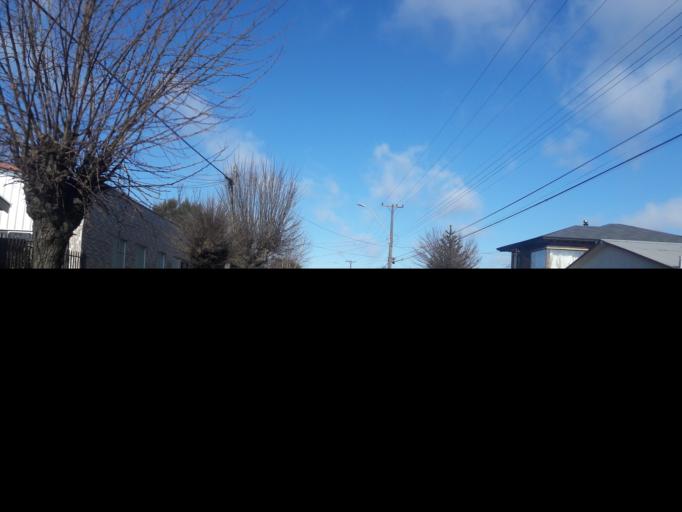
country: CL
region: Araucania
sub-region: Provincia de Malleco
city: Victoria
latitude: -38.2378
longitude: -72.3294
